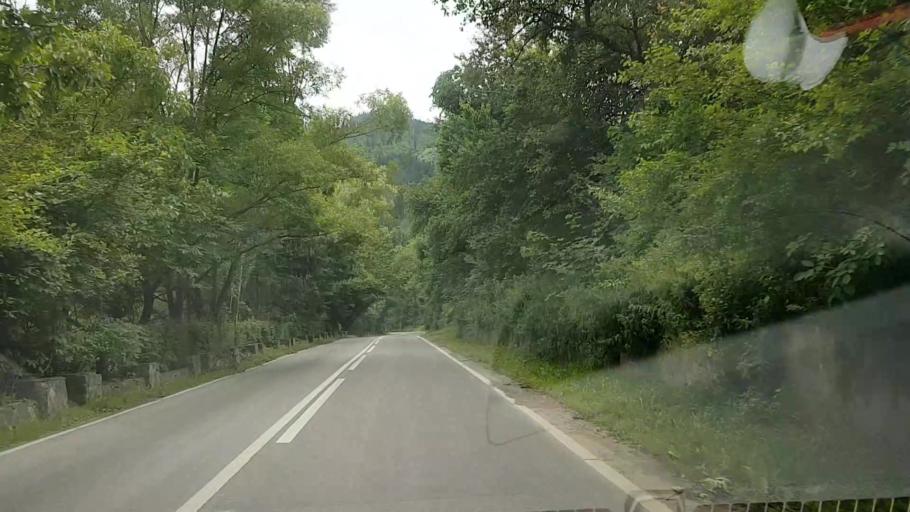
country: RO
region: Neamt
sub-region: Comuna Poiana Teiului
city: Poiana Teiului
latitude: 47.0993
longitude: 25.9415
